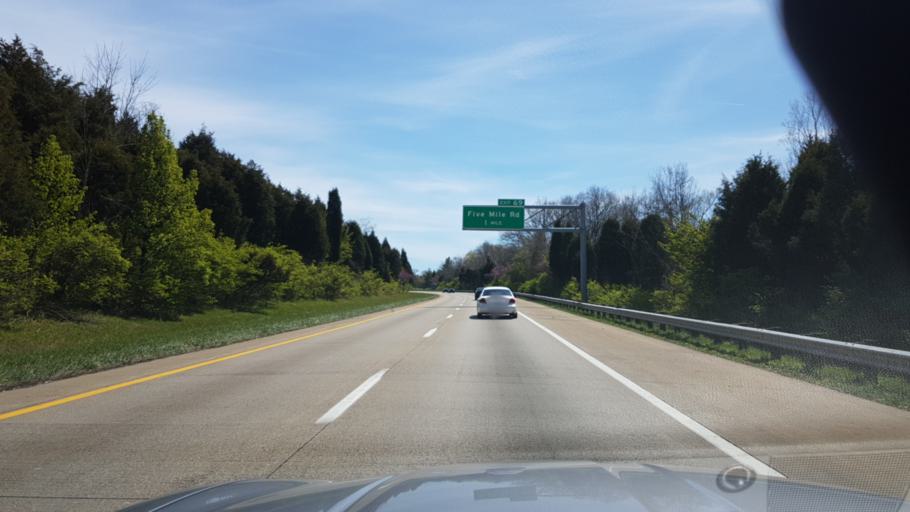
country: US
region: Ohio
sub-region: Hamilton County
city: Salem Heights
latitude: 39.0563
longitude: -84.3789
